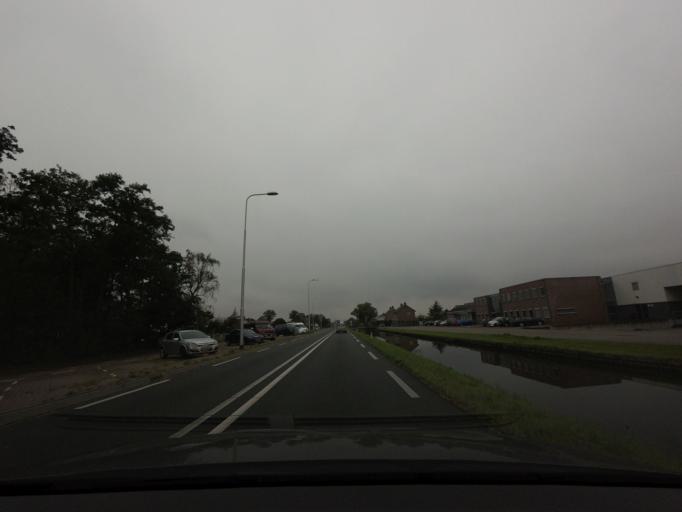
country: NL
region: South Holland
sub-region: Gemeente Noordwijkerhout
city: Noordwijkerhout
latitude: 52.2414
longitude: 4.5010
